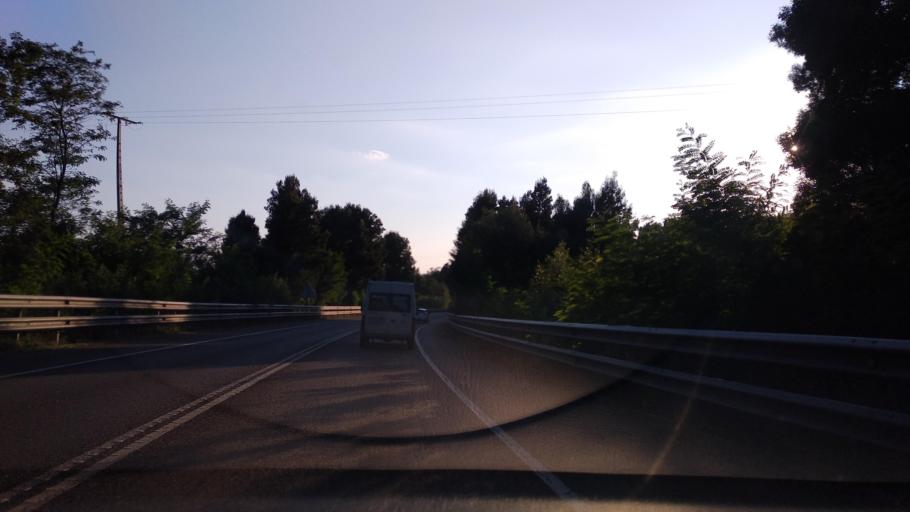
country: ES
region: Galicia
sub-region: Provincia de Pontevedra
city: Moana
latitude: 42.2730
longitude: -8.7589
